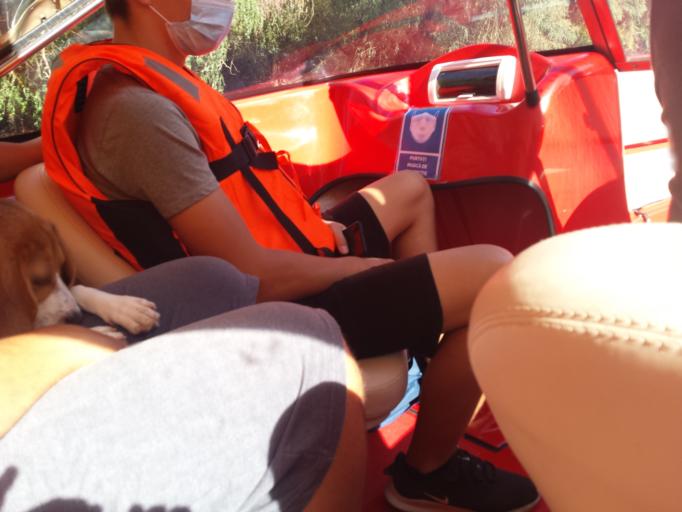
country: RO
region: Tulcea
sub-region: Comuna Pardina
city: Pardina
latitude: 45.2427
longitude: 28.9206
